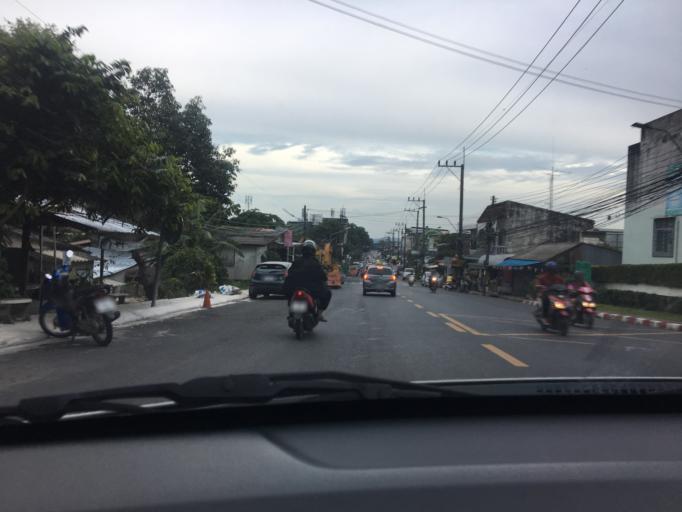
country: TH
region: Phuket
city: Phuket
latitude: 7.8886
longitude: 98.3982
